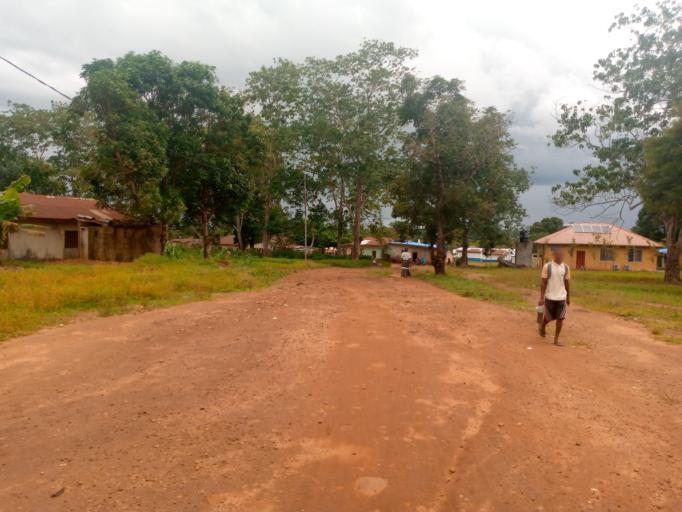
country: SL
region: Southern Province
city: Mogbwemo
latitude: 7.6035
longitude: -12.1736
